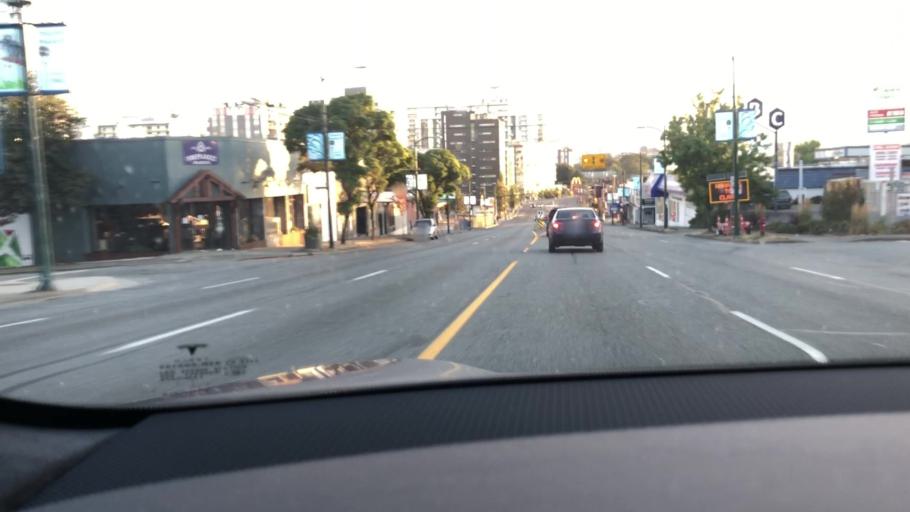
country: CA
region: British Columbia
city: Vancouver
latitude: 49.2671
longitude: -123.1008
